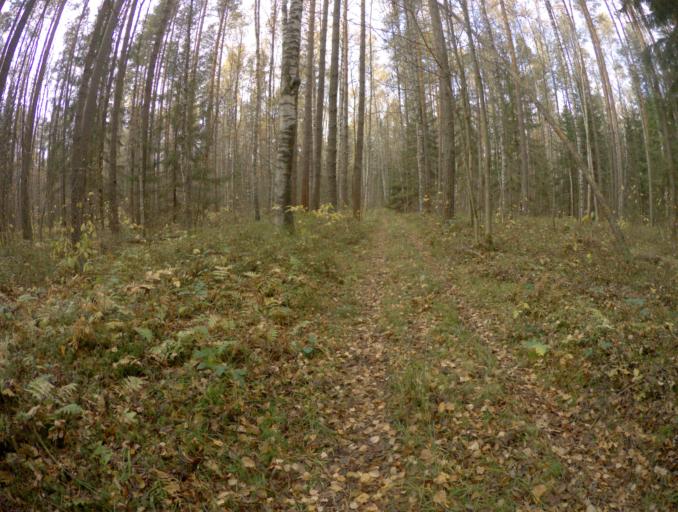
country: RU
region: Vladimir
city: Raduzhnyy
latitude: 55.9646
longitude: 40.3646
